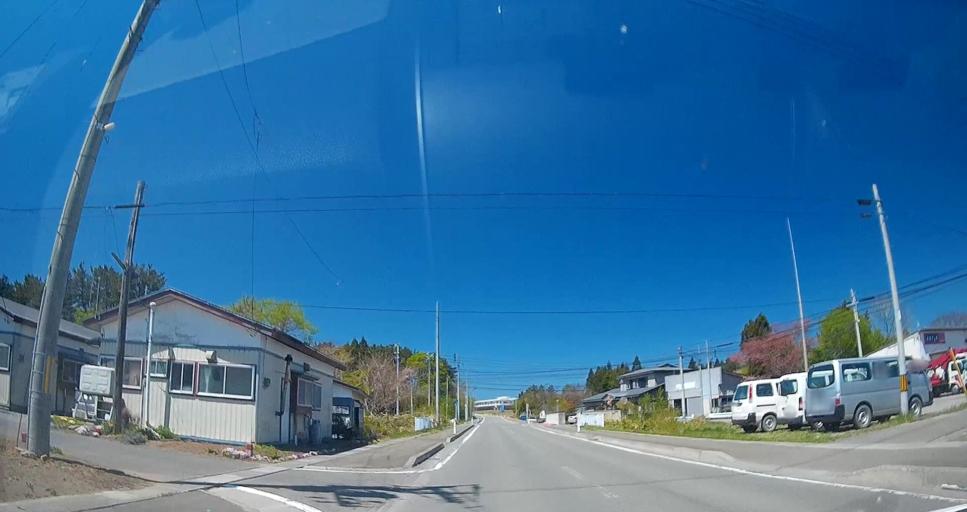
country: JP
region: Aomori
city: Misawa
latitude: 40.9687
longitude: 141.3745
